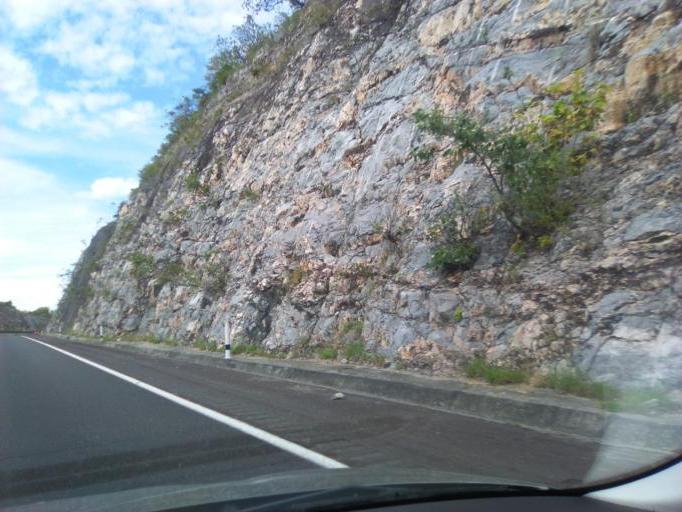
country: MX
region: Guerrero
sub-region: Eduardo Neri
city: Axaxacualco
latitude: 17.7869
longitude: -99.4848
